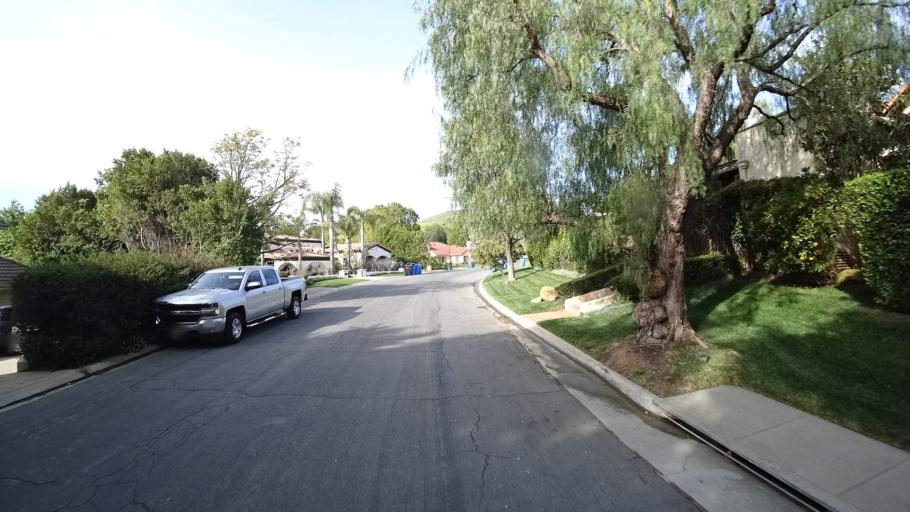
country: US
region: California
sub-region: Ventura County
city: Oak Park
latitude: 34.1882
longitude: -118.7883
